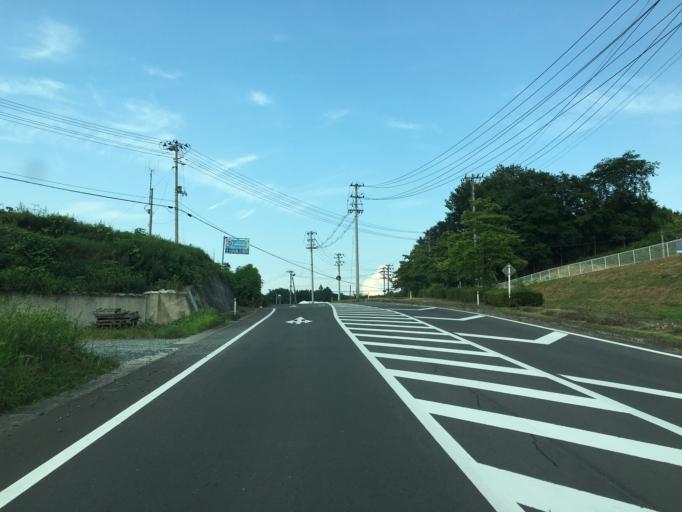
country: JP
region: Fukushima
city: Nihommatsu
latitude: 37.5747
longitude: 140.4316
